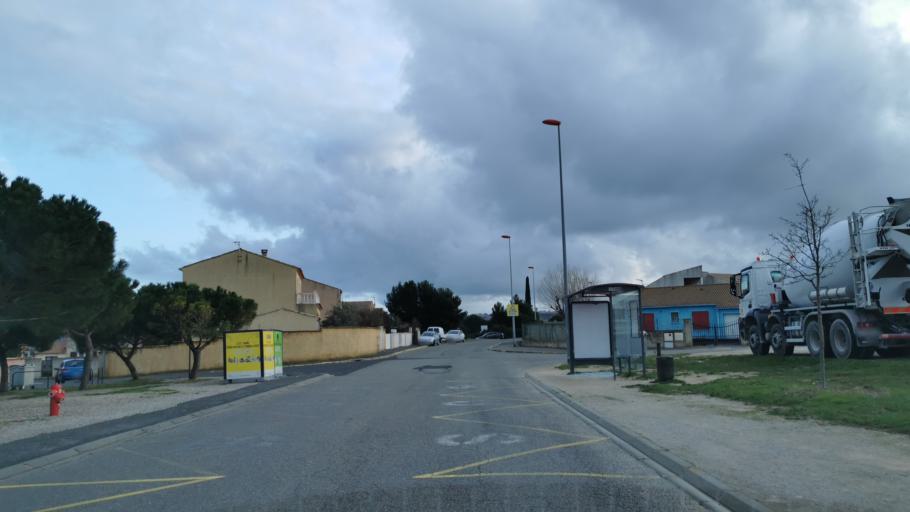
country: FR
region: Languedoc-Roussillon
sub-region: Departement de l'Aude
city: Narbonne
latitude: 43.1872
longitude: 2.9754
